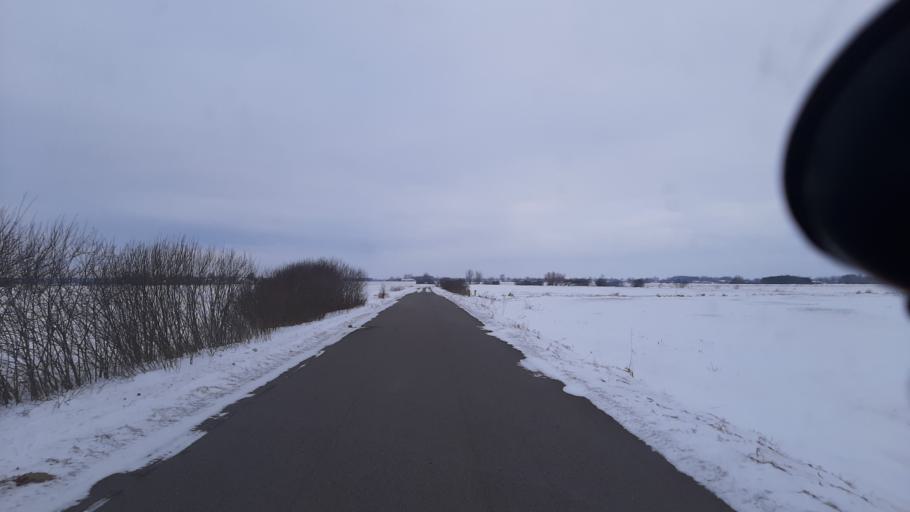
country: PL
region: Lublin Voivodeship
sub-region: Powiat lubartowski
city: Abramow
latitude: 51.4383
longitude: 22.3116
